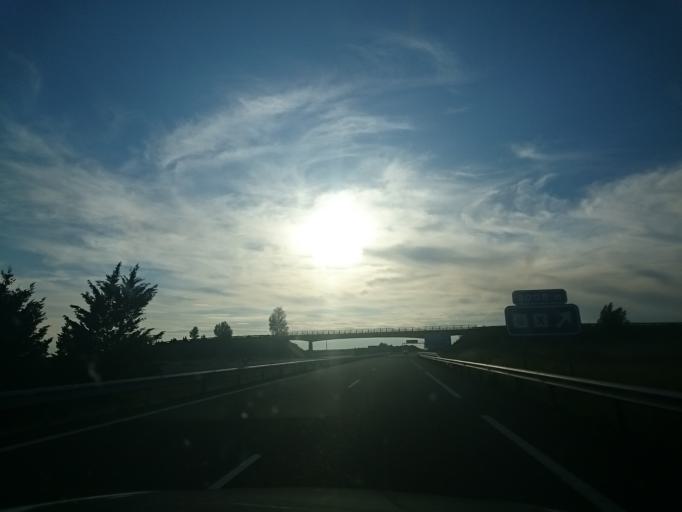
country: ES
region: Castille and Leon
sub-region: Provincia de Leon
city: Sahagun
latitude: 42.3776
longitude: -5.0094
